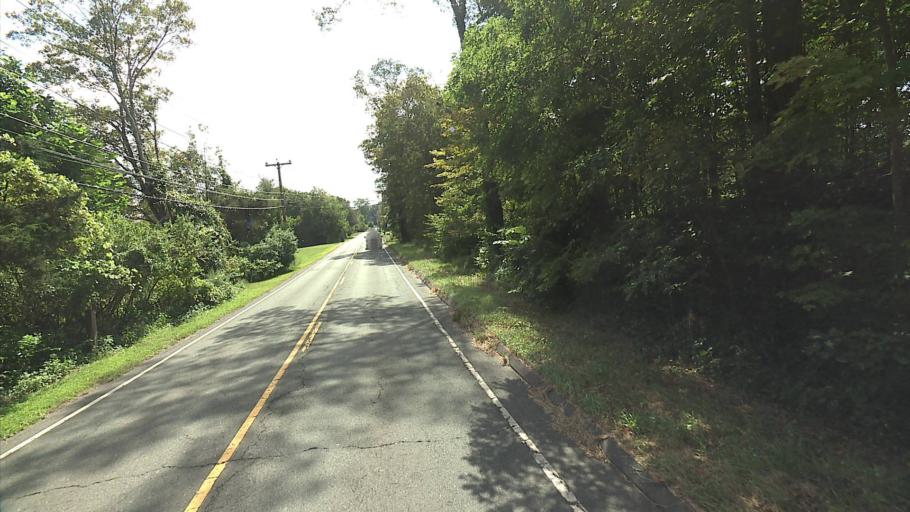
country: US
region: Connecticut
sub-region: Hartford County
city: North Granby
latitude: 41.9832
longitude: -72.8204
